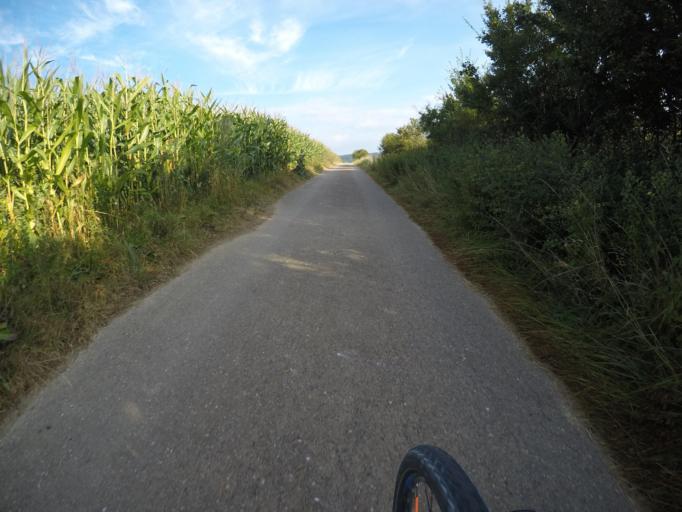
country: DE
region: Baden-Wuerttemberg
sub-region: Regierungsbezirk Stuttgart
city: Herbrechtingen
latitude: 48.6171
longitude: 10.2038
